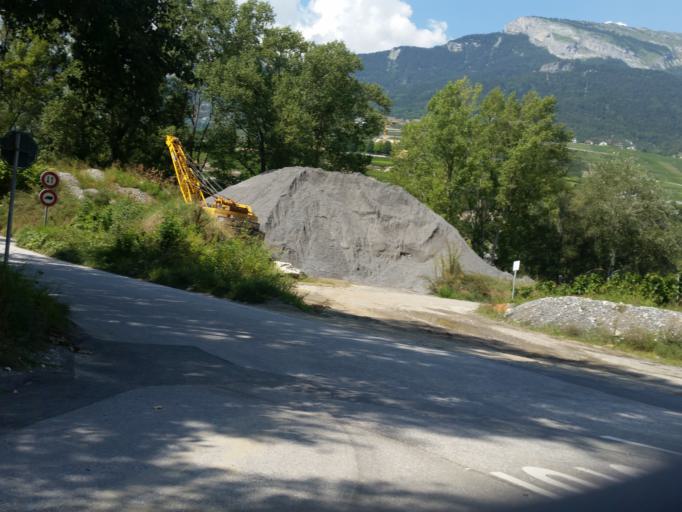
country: CH
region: Valais
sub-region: Conthey District
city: Conthey
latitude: 46.2325
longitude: 7.3124
